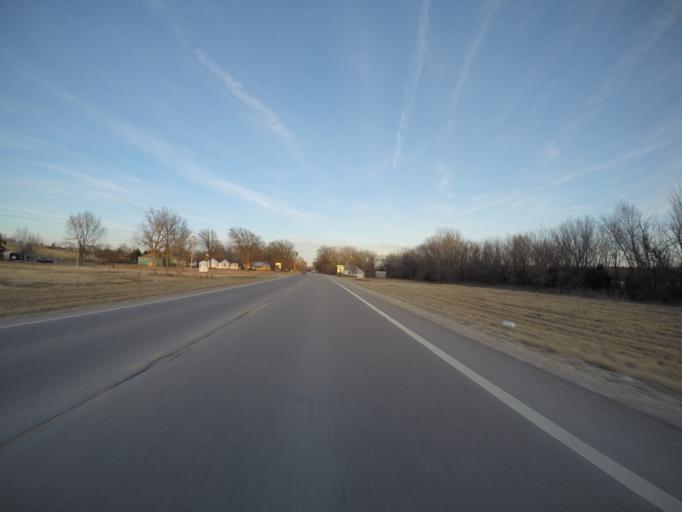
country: US
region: Kansas
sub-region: Morris County
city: Council Grove
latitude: 38.6552
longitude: -96.5108
